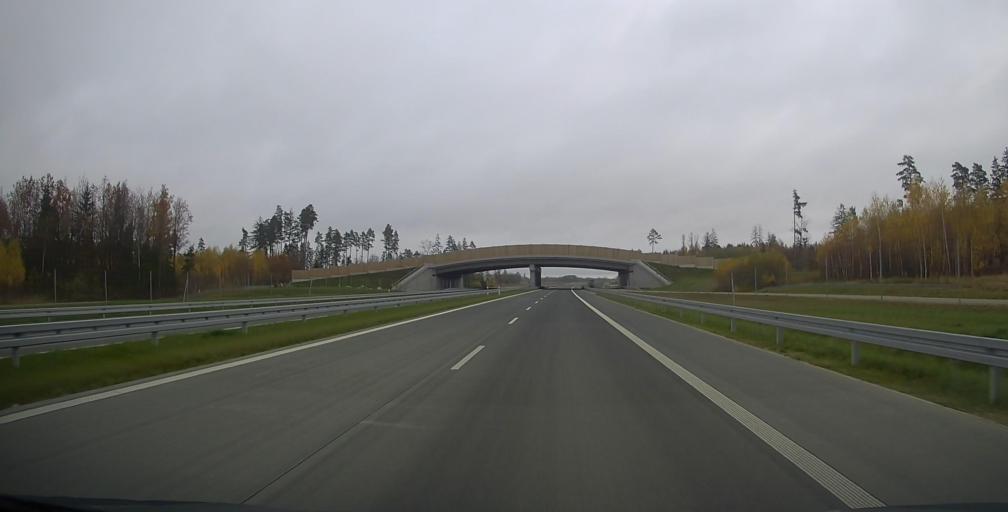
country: PL
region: Podlasie
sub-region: Powiat suwalski
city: Raczki
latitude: 53.8981
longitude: 22.6906
